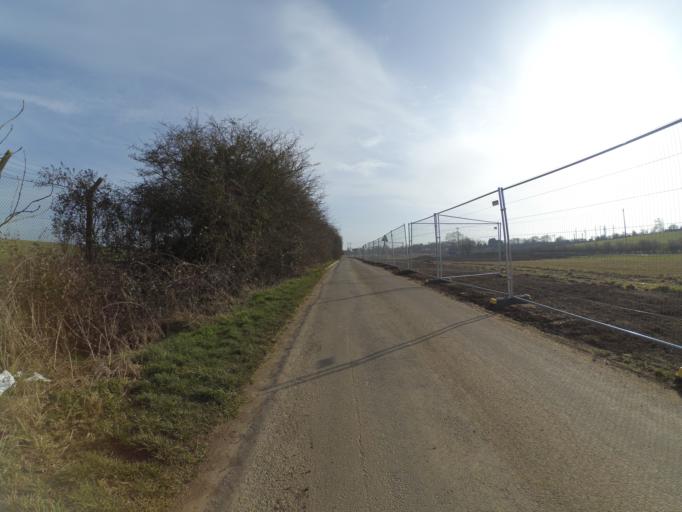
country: GB
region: England
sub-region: Warwickshire
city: Rugby
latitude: 52.3603
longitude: -1.2004
